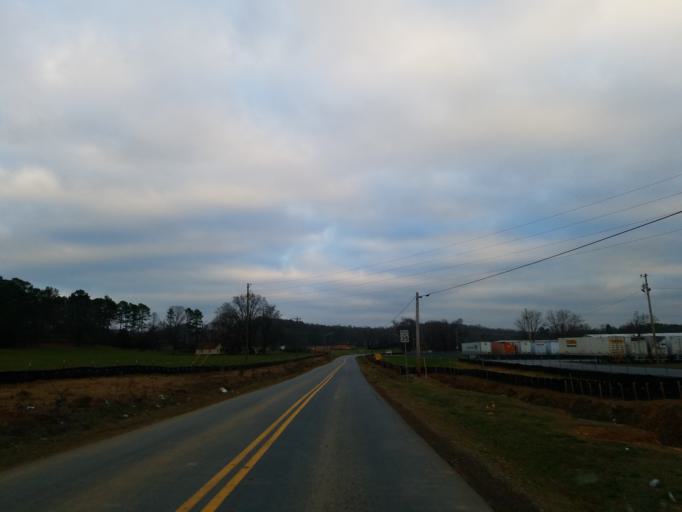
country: US
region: Georgia
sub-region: Gordon County
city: Calhoun
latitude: 34.4420
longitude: -84.9112
